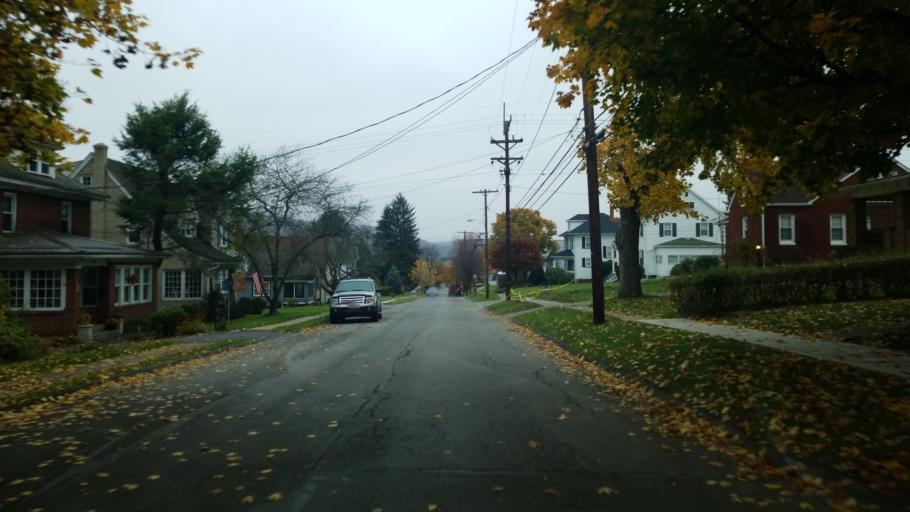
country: US
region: Pennsylvania
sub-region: Clearfield County
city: Clearfield
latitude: 41.0122
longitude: -78.4340
